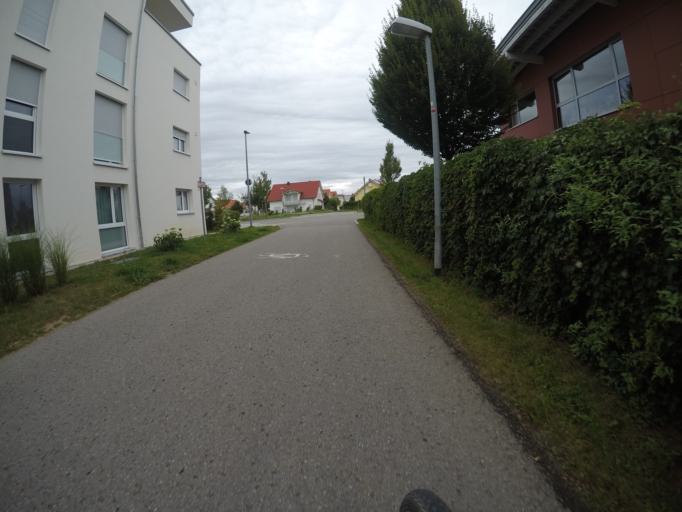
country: DE
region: Baden-Wuerttemberg
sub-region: Regierungsbezirk Stuttgart
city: Holzgerlingen
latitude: 48.6421
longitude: 9.0051
